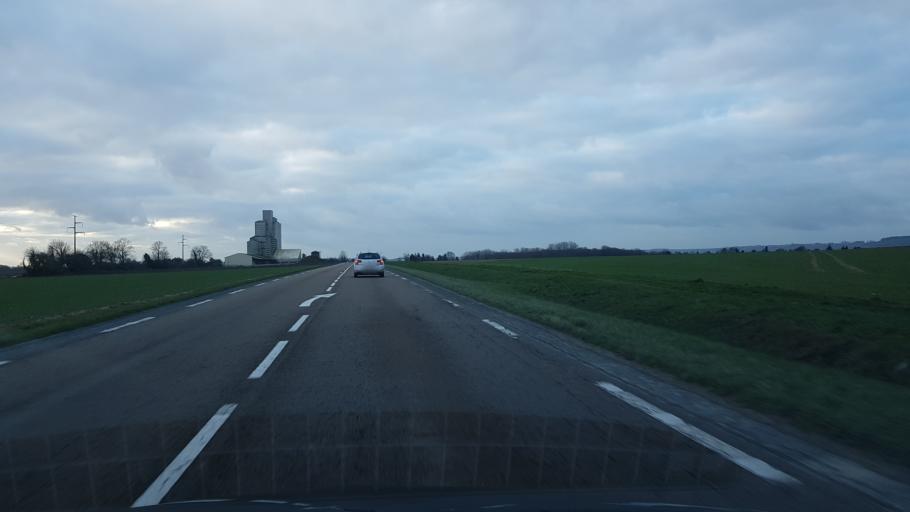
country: FR
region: Champagne-Ardenne
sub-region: Departement de la Marne
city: Connantre
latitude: 48.7268
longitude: 3.8612
